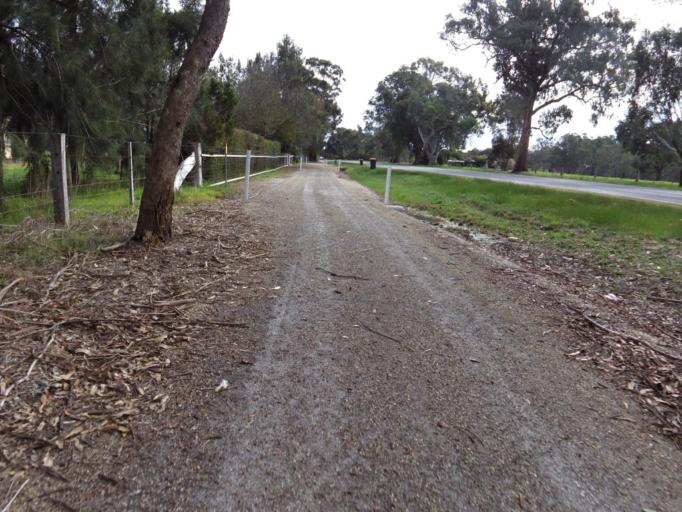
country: AU
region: Victoria
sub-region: Wangaratta
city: Wangaratta
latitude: -36.4017
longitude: 146.3472
